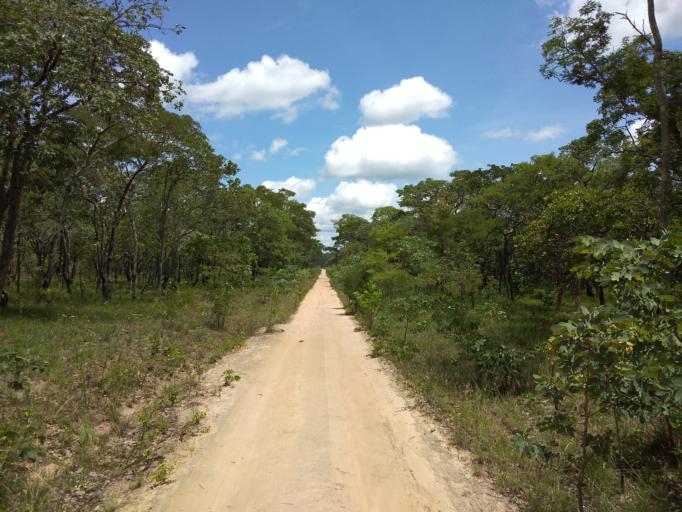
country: ZM
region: Central
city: Mkushi
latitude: -13.9555
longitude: 29.8829
